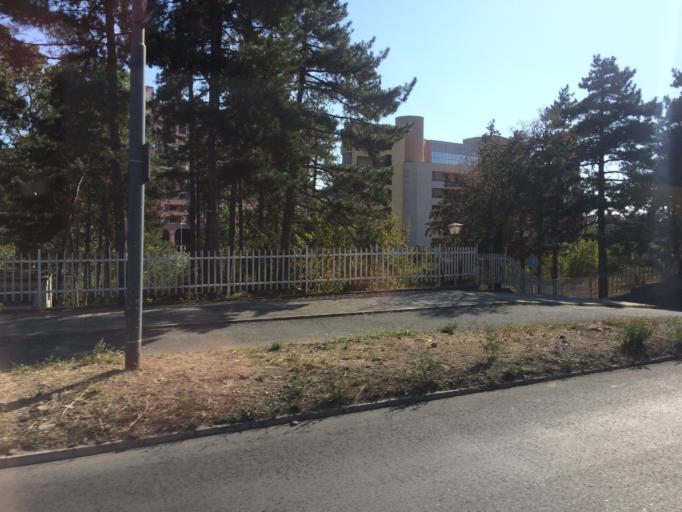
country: BG
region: Burgas
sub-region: Obshtina Nesebur
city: Sveti Vlas
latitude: 42.7103
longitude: 27.7262
